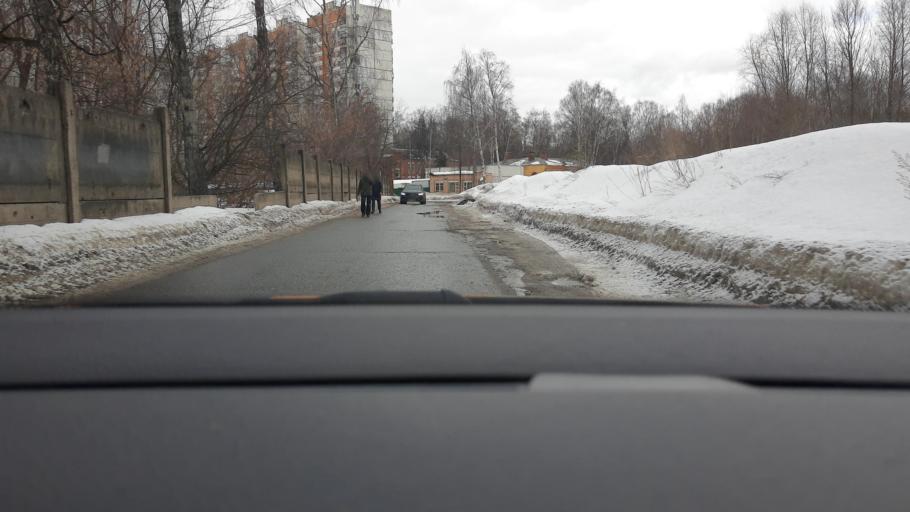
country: RU
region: Moscow
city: Babushkin
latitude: 55.8530
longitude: 37.7016
